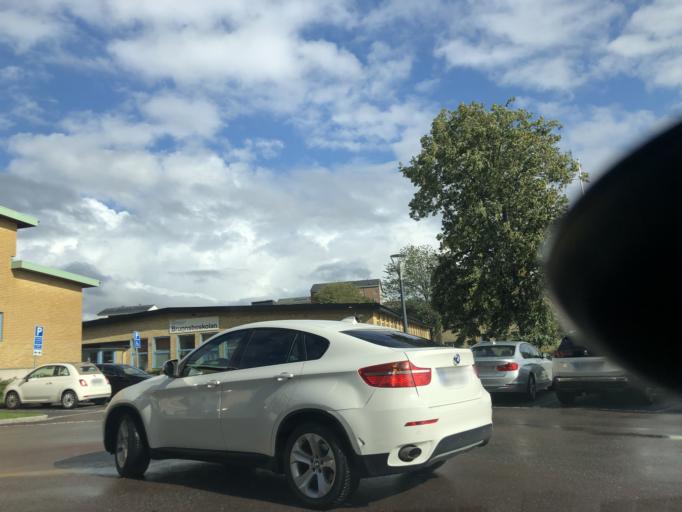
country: SE
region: Vaestra Goetaland
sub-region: Goteborg
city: Goeteborg
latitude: 57.7304
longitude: 11.9680
